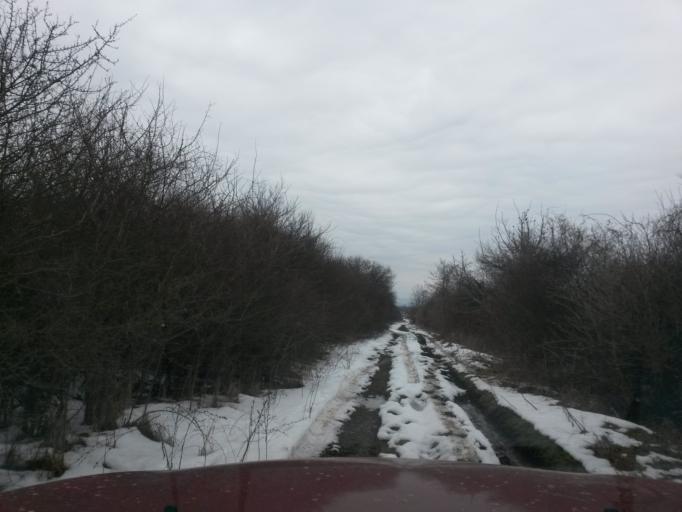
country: SK
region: Kosicky
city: Vinne
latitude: 48.7418
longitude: 22.0248
